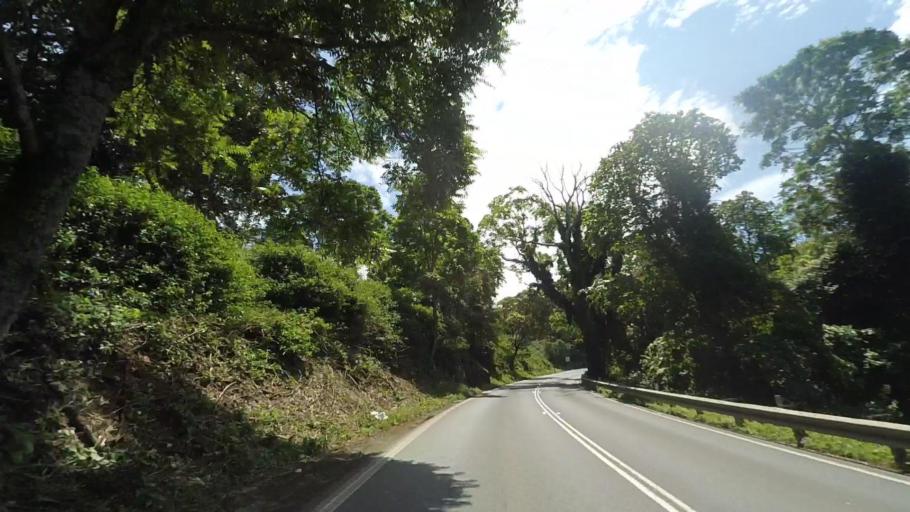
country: AU
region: New South Wales
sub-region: Kiama
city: Gerringong
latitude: -34.7461
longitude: 150.7734
